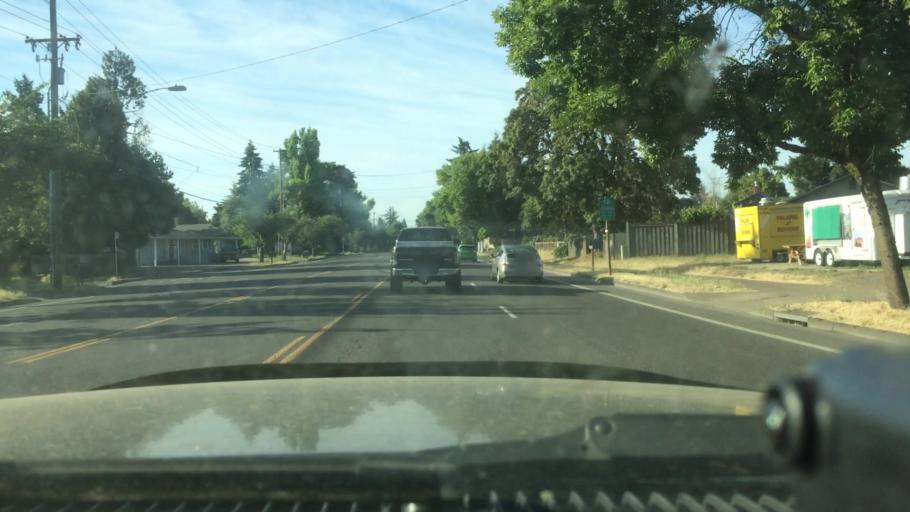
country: US
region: Oregon
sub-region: Lane County
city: Eugene
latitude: 44.0933
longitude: -123.1272
